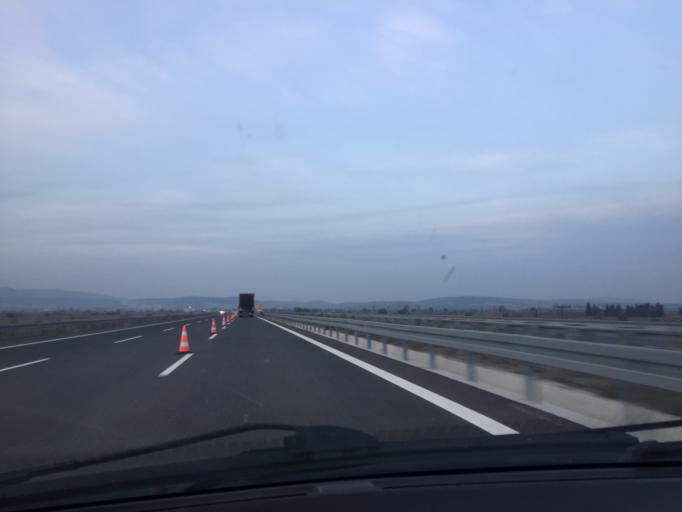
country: TR
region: Manisa
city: Halitpasa
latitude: 38.7399
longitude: 27.6580
